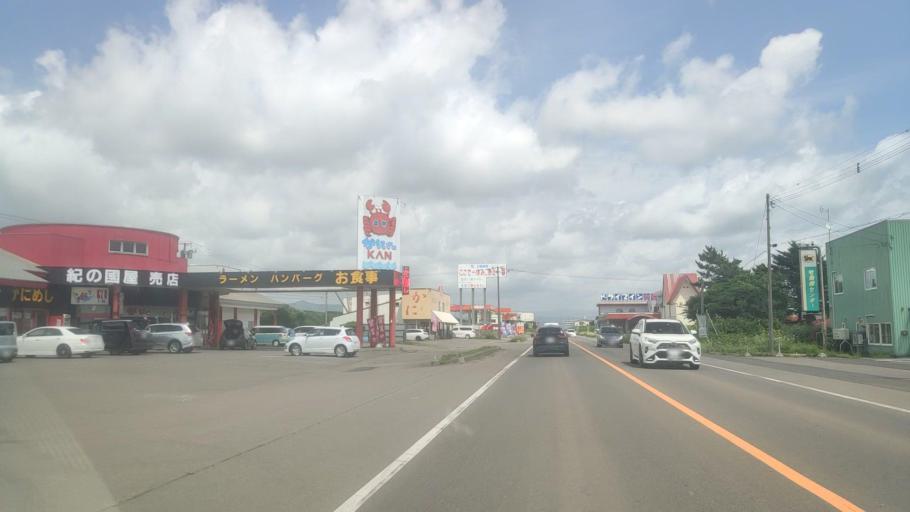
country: JP
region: Hokkaido
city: Niseko Town
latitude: 42.4914
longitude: 140.3587
